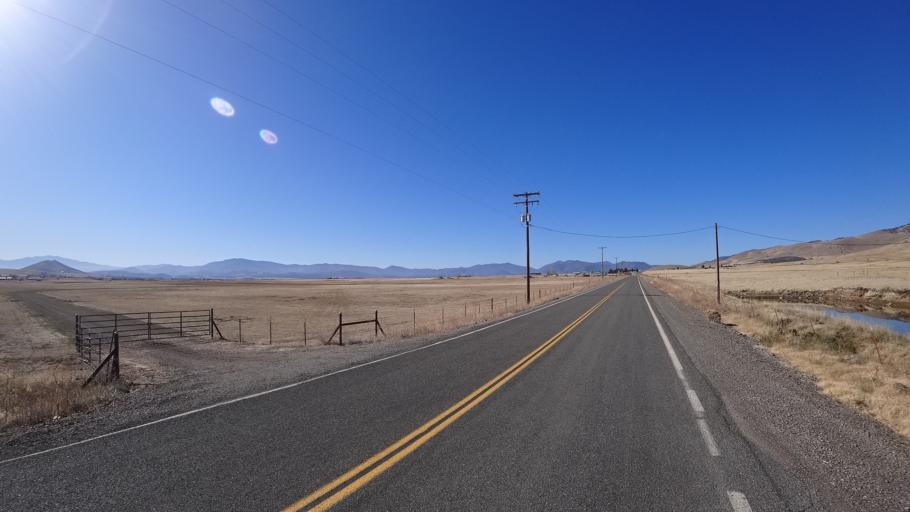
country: US
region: California
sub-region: Siskiyou County
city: Montague
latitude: 41.7707
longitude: -122.5054
